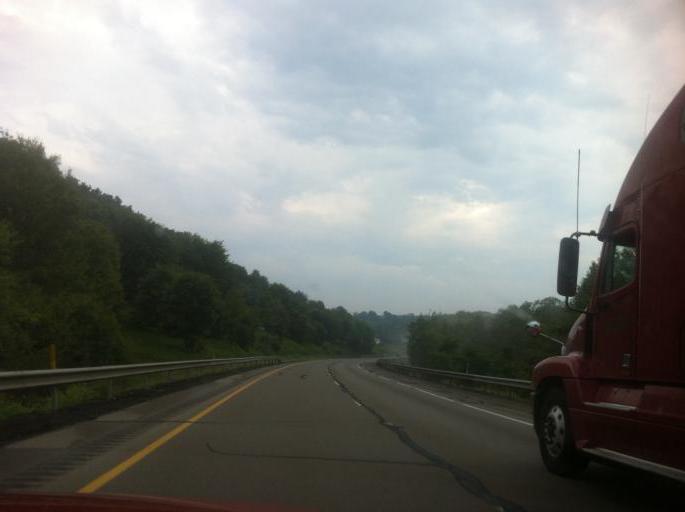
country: US
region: Pennsylvania
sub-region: Jefferson County
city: Brookville
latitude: 41.1701
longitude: -79.0209
